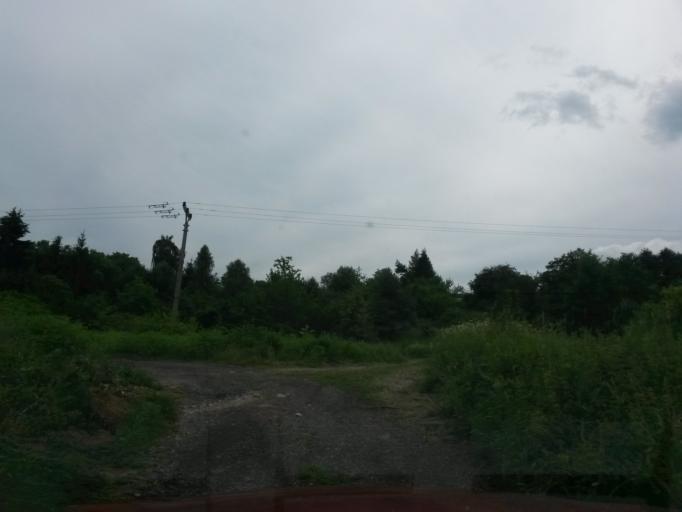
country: SK
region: Nitriansky
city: Handlova
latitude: 48.7349
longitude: 18.7475
